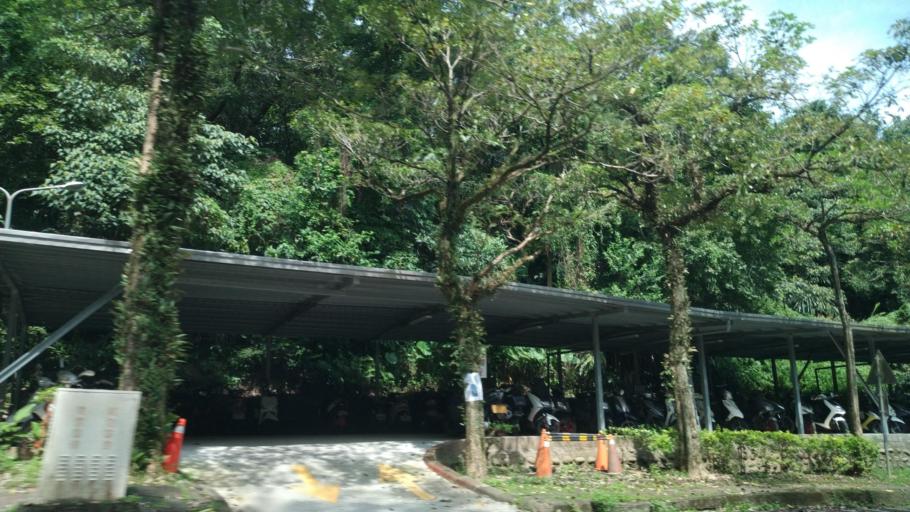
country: TW
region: Taipei
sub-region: Taipei
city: Banqiao
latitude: 24.9513
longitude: 121.5089
